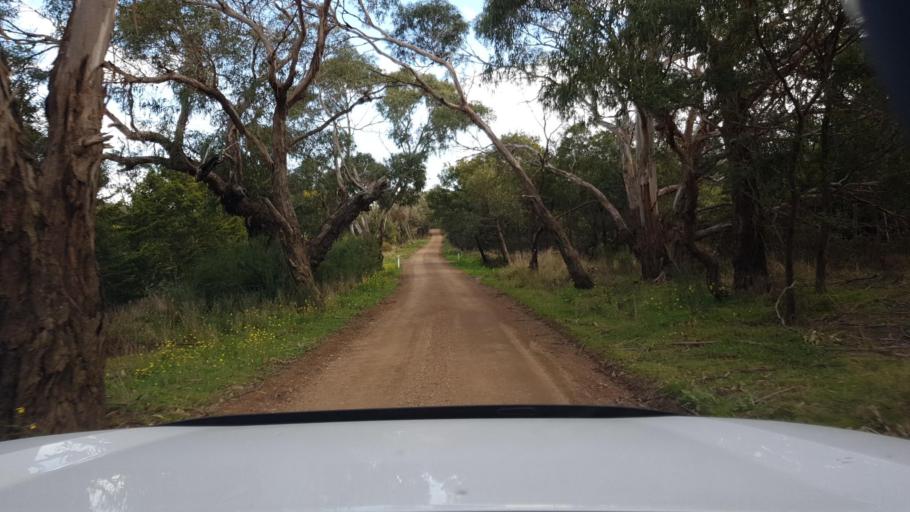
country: AU
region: Victoria
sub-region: Hume
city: Sunbury
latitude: -37.5652
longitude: 144.6184
